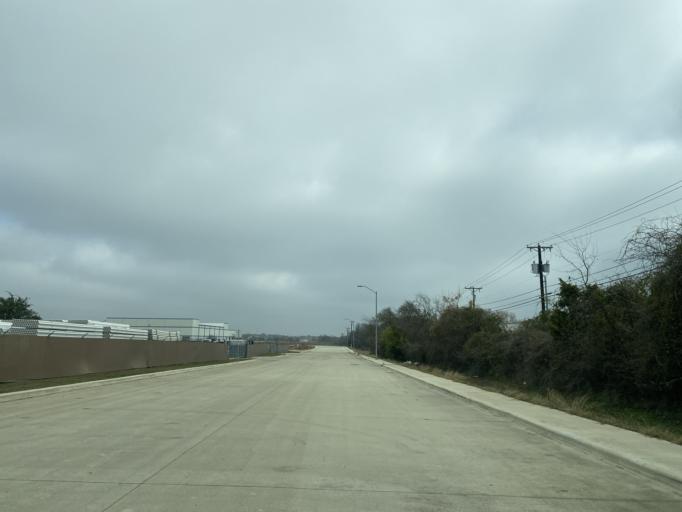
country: US
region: Texas
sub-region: Williamson County
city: Round Rock
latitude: 30.5378
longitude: -97.6870
